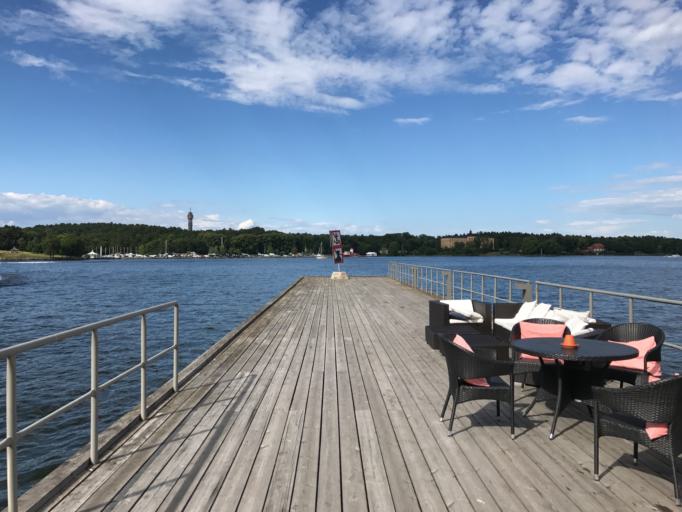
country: SE
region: Stockholm
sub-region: Nacka Kommun
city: Nacka
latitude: 59.3161
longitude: 18.1245
